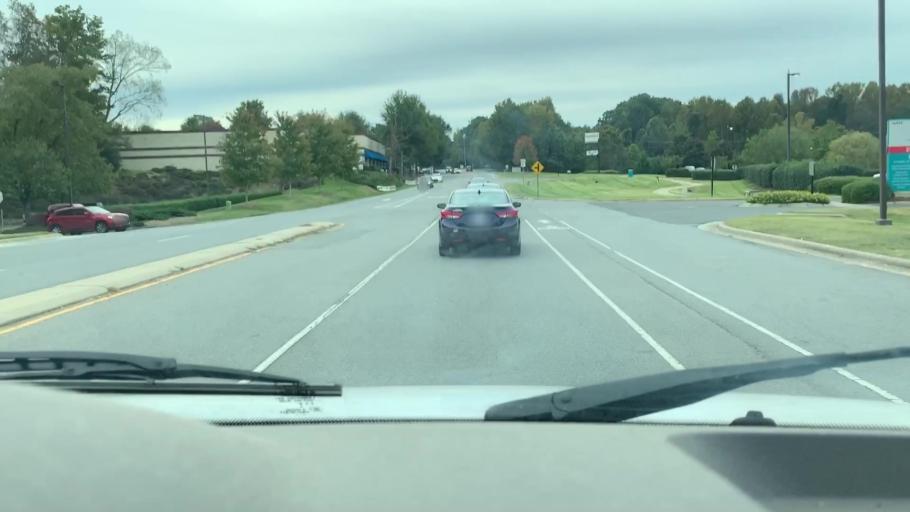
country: US
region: North Carolina
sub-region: Mecklenburg County
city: Huntersville
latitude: 35.4392
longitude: -80.8654
